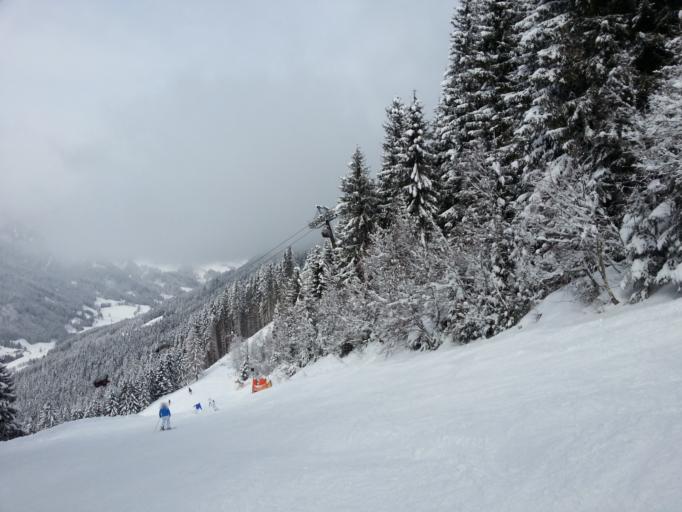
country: AT
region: Salzburg
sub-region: Politischer Bezirk Sankt Johann im Pongau
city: Kleinarl
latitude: 47.2830
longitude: 13.3298
